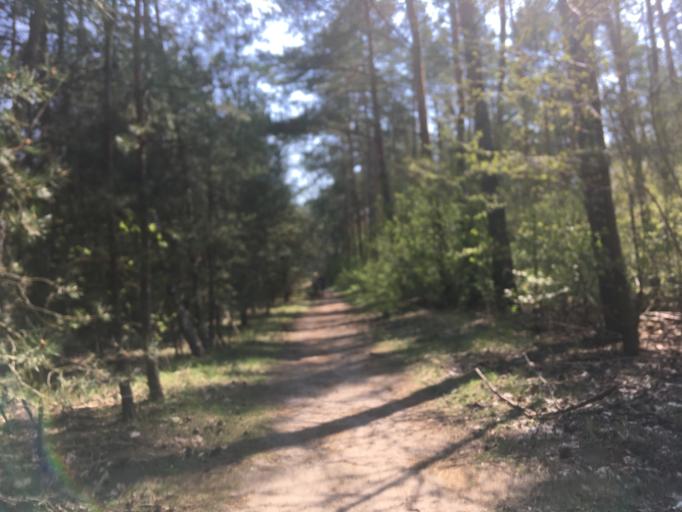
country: DE
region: Berlin
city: Grunewald
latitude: 52.4770
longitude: 13.2283
